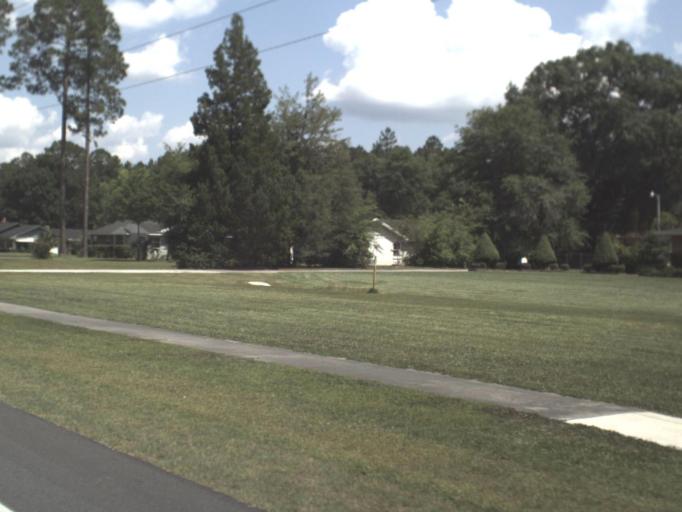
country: US
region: Florida
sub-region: Bradford County
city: Starke
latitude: 29.9399
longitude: -82.0942
